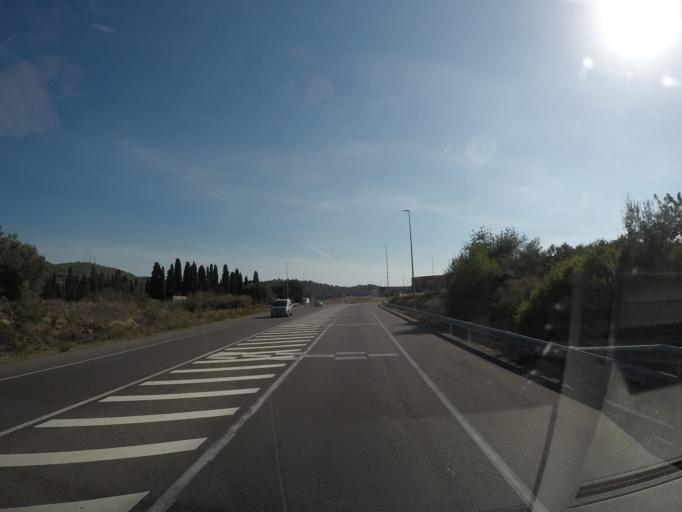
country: ES
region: Catalonia
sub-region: Provincia de Tarragona
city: El Perello
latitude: 40.8829
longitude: 0.7185
